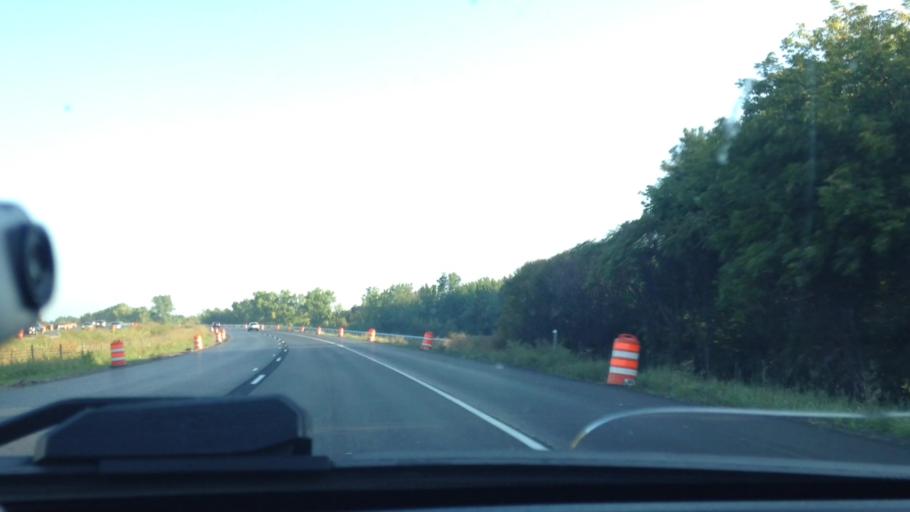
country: US
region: Wisconsin
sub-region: Brown County
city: Suamico
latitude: 44.6364
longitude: -88.0458
